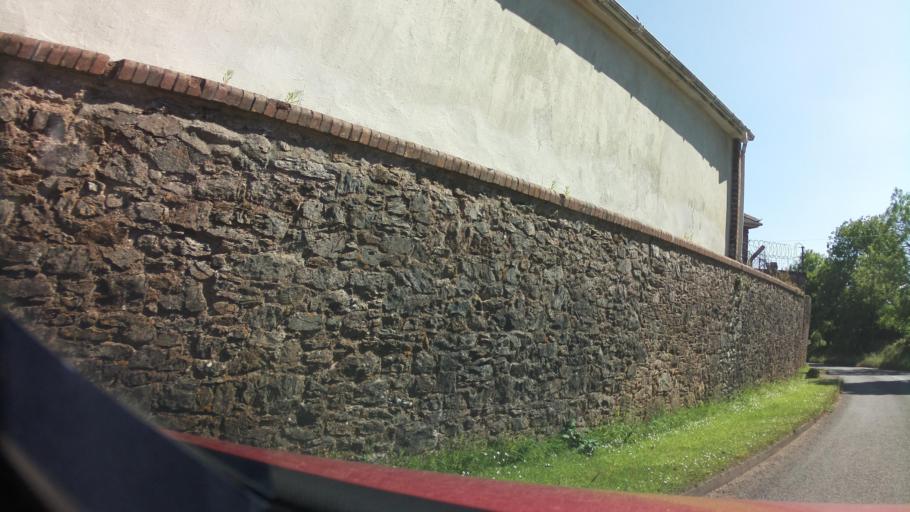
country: GB
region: England
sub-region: Devon
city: Marldon
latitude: 50.4180
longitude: -3.6096
